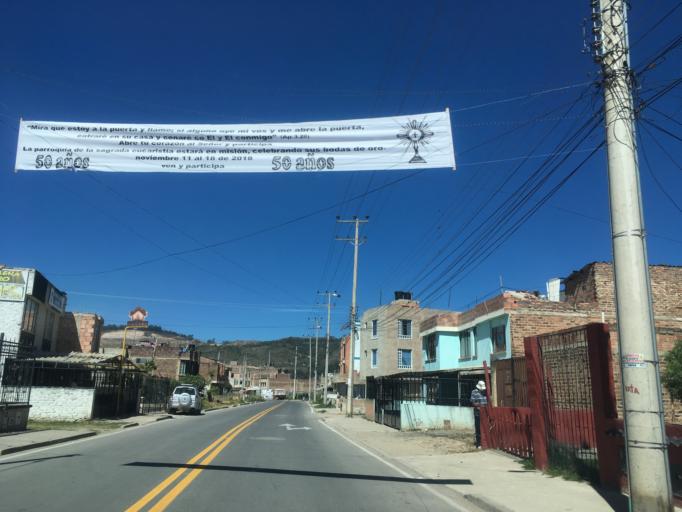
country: CO
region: Boyaca
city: Sogamoso
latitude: 5.7107
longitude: -72.9445
